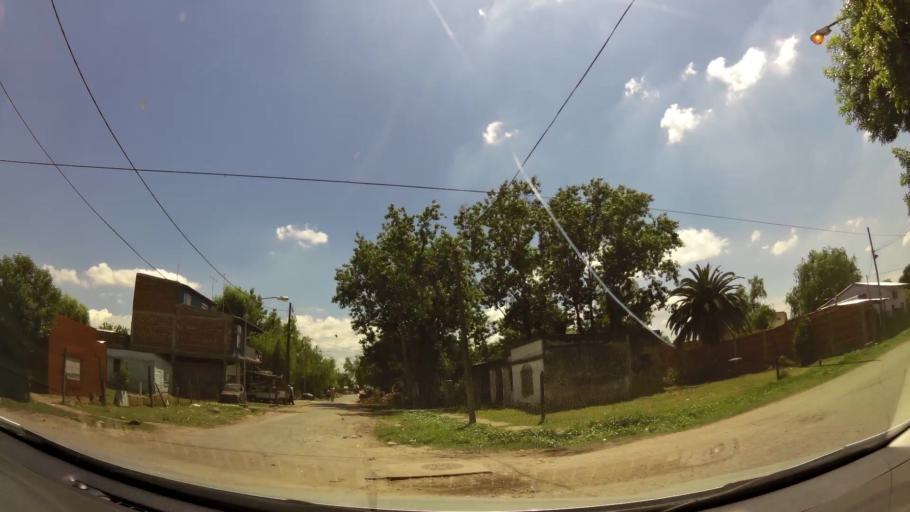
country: AR
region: Buenos Aires
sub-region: Partido de Tigre
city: Tigre
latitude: -34.4402
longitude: -58.5895
